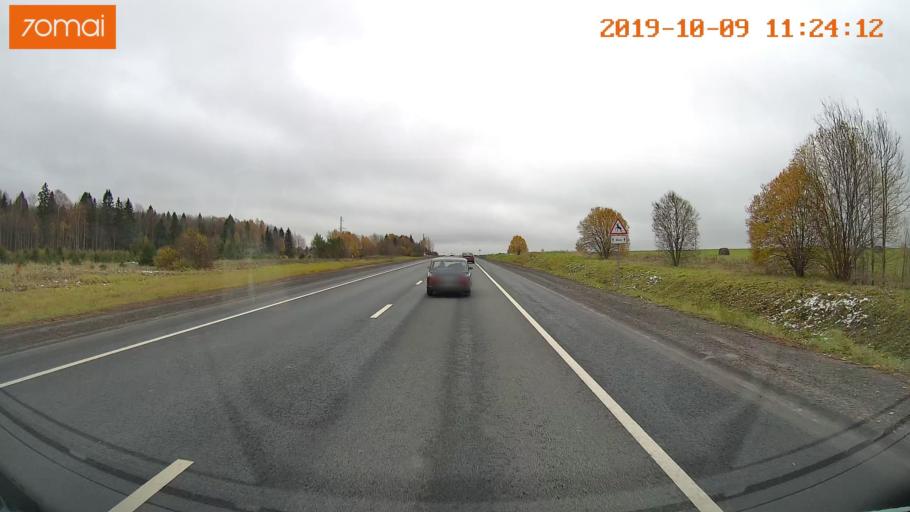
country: RU
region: Vologda
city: Vologda
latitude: 59.1137
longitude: 39.9776
